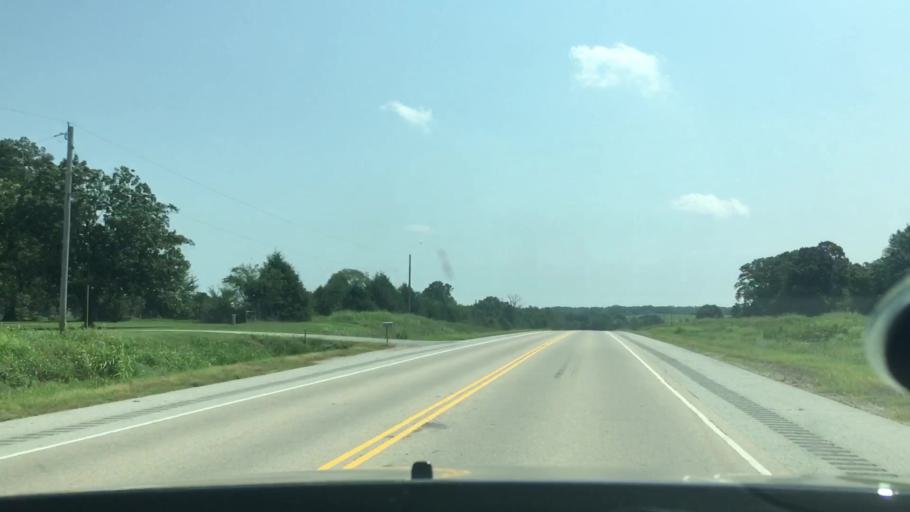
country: US
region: Oklahoma
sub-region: Atoka County
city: Atoka
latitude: 34.2889
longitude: -95.9663
